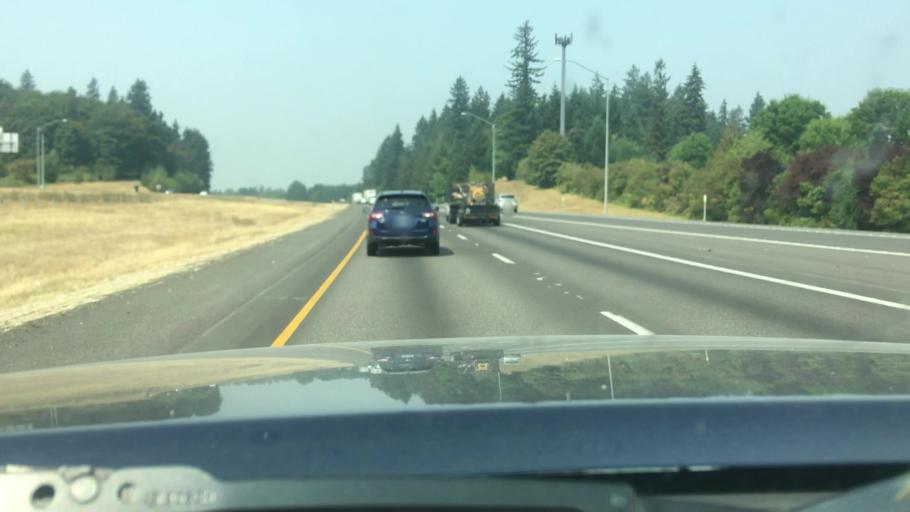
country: US
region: Oregon
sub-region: Clackamas County
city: Stafford
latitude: 45.3718
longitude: -122.7109
